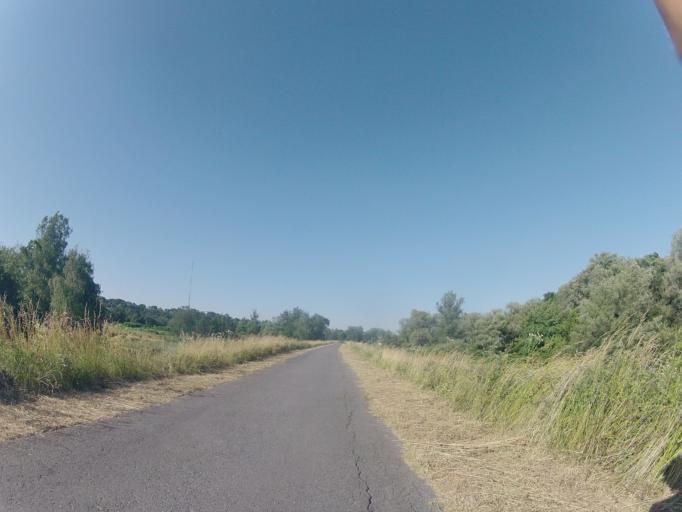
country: PL
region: Lesser Poland Voivodeship
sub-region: Krakow
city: Krakow
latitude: 50.0442
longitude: 19.8995
